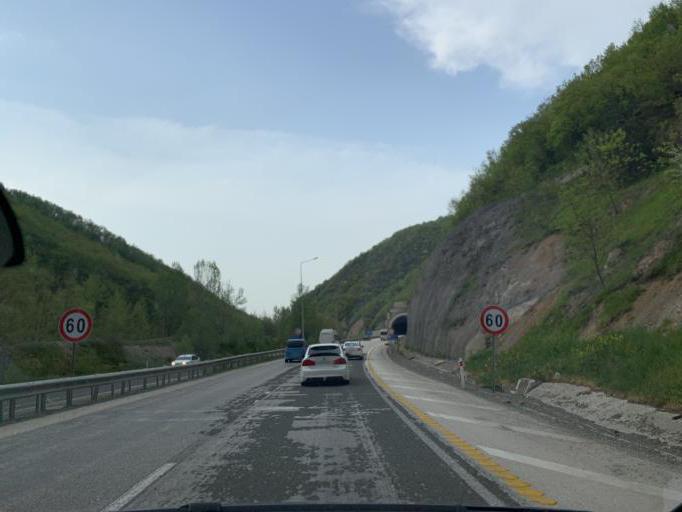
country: TR
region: Bursa
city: Kursunlu
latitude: 40.0034
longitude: 29.6520
